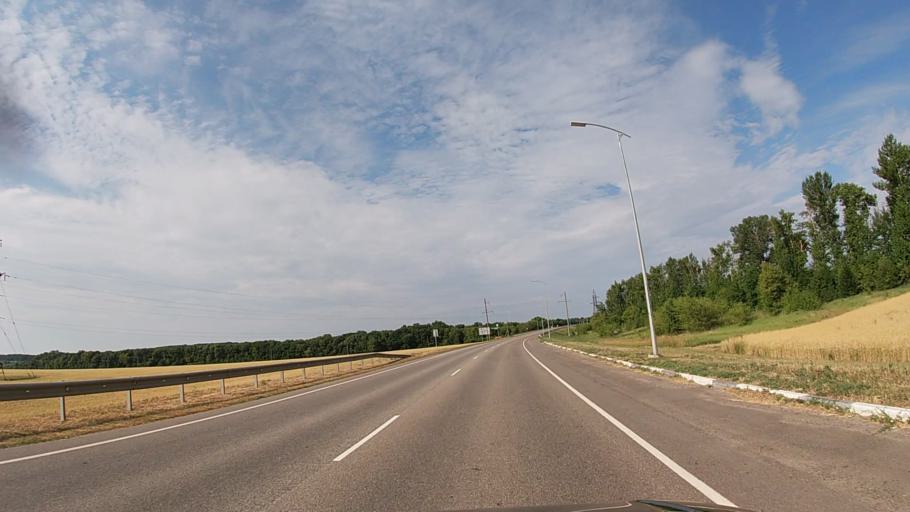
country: RU
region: Belgorod
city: Proletarskiy
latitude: 50.8060
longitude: 35.7423
